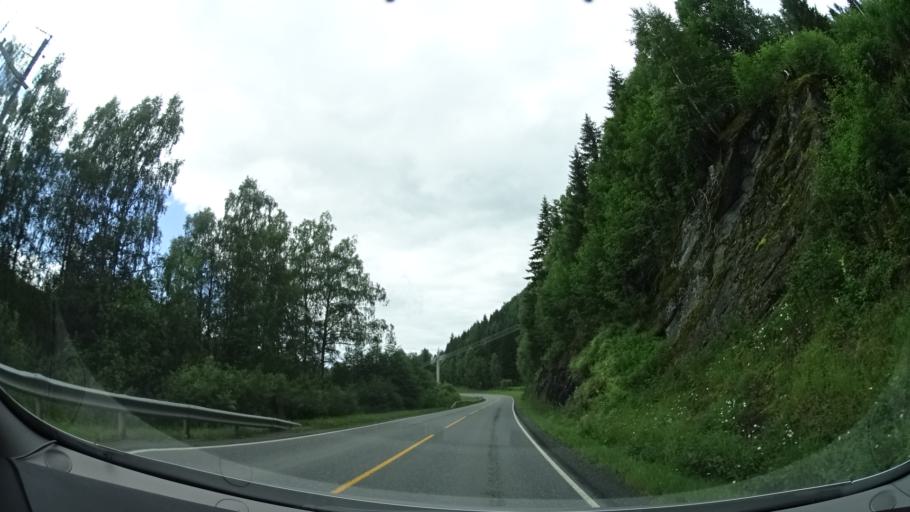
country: NO
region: Nord-Trondelag
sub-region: Meraker
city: Meraker
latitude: 63.4042
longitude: 11.7694
